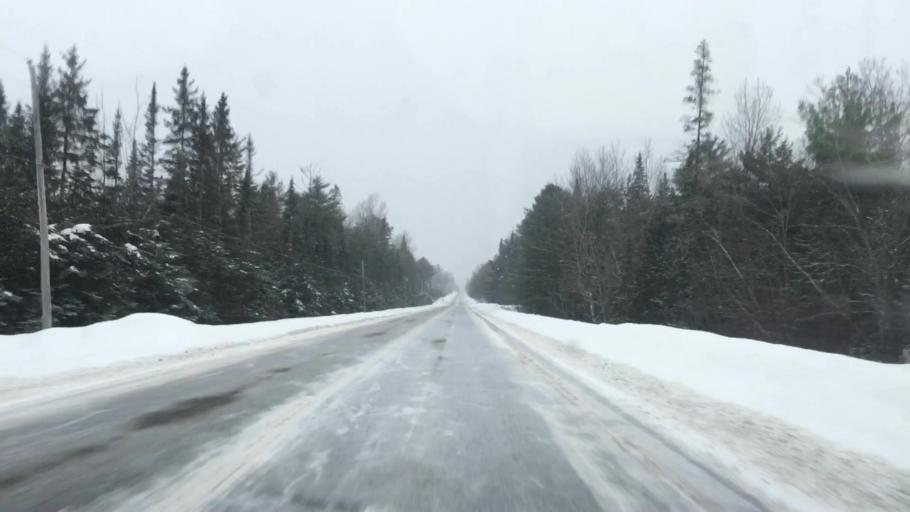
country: US
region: Maine
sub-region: Penobscot County
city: Medway
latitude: 45.5273
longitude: -68.3586
